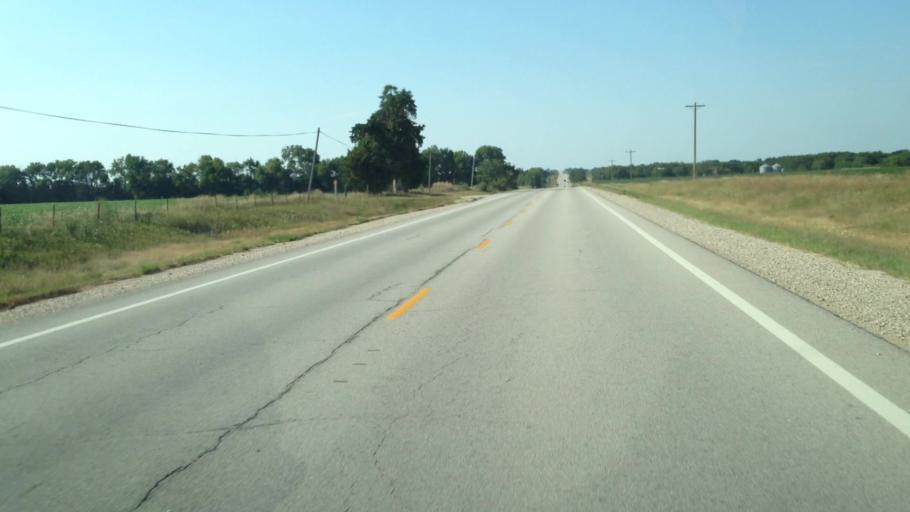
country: US
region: Kansas
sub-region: Anderson County
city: Garnett
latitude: 38.1004
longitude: -95.2430
